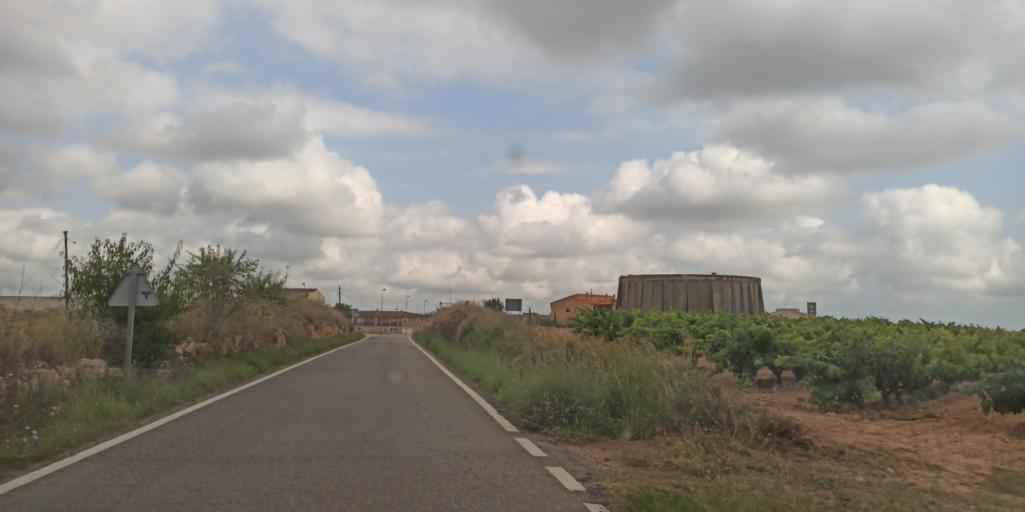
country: ES
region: Catalonia
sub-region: Provincia de Tarragona
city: Sant Jaume dels Domenys
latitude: 41.3034
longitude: 1.5576
